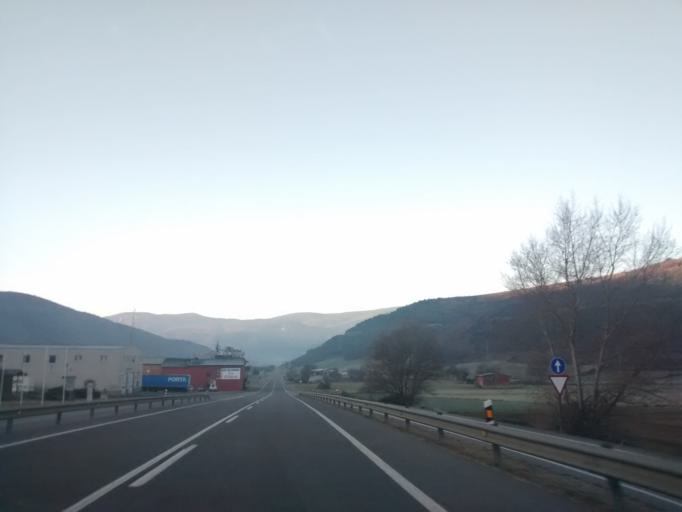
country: ES
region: Catalonia
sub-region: Provincia de Lleida
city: la Seu d'Urgell
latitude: 42.3422
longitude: 1.4220
